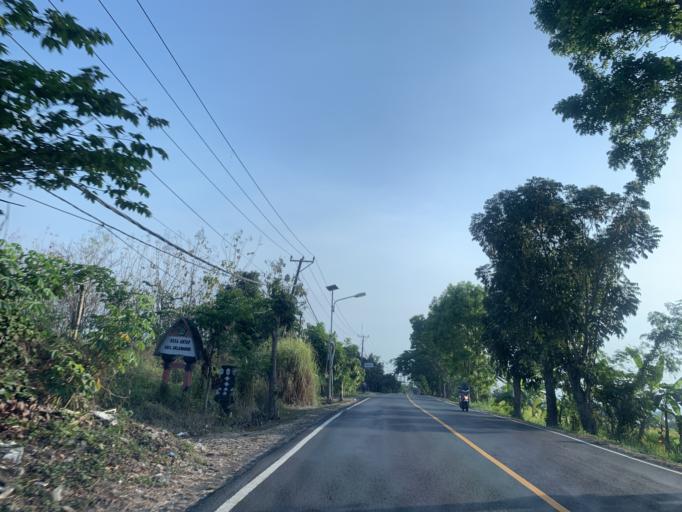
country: ID
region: Bali
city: Banjar Gablogan
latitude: -8.5129
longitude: 115.0162
